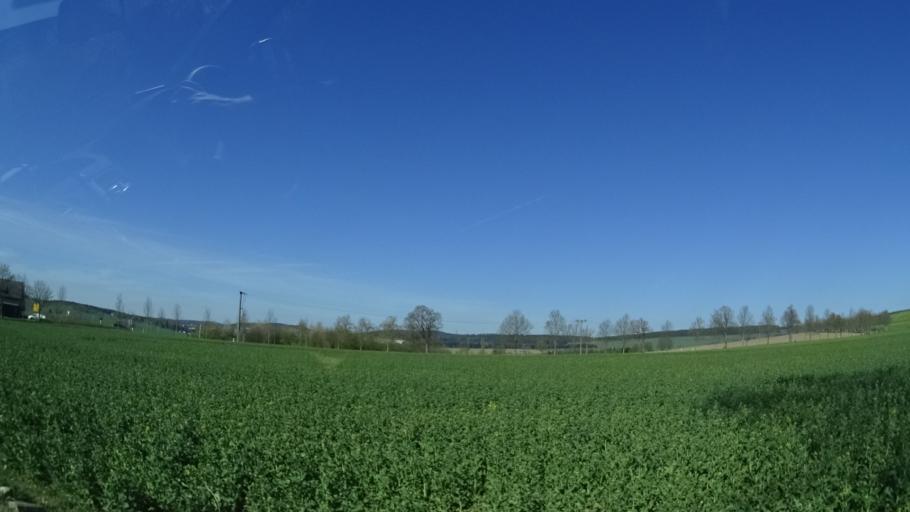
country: DE
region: Thuringia
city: Bohlen
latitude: 50.5914
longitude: 11.0426
